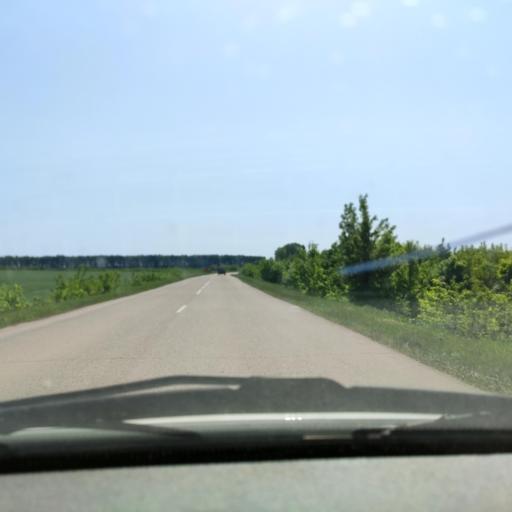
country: RU
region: Bashkortostan
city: Avdon
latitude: 54.5280
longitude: 55.6390
